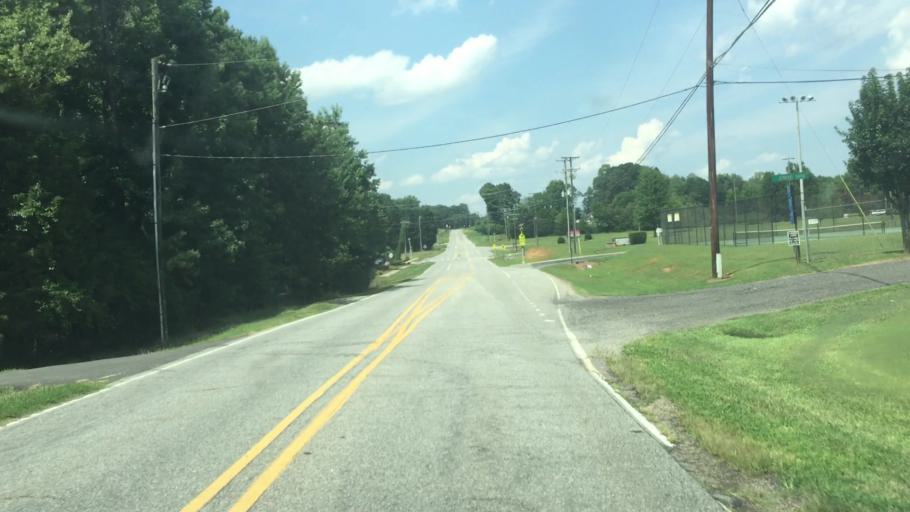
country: US
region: North Carolina
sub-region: Iredell County
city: Mooresville
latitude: 35.5533
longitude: -80.7909
